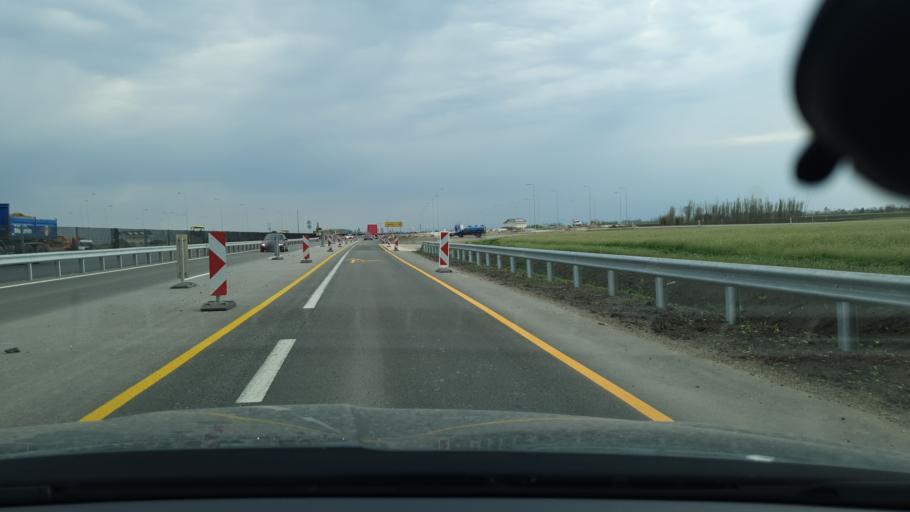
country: HU
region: Pest
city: Abony
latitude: 47.2168
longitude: 19.9801
